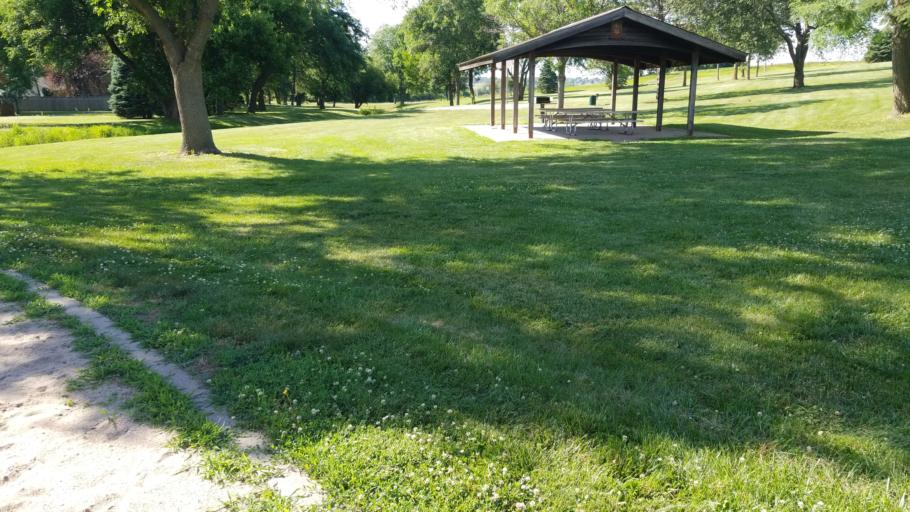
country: US
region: Nebraska
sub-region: Sarpy County
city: Papillion
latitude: 41.1419
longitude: -96.0190
